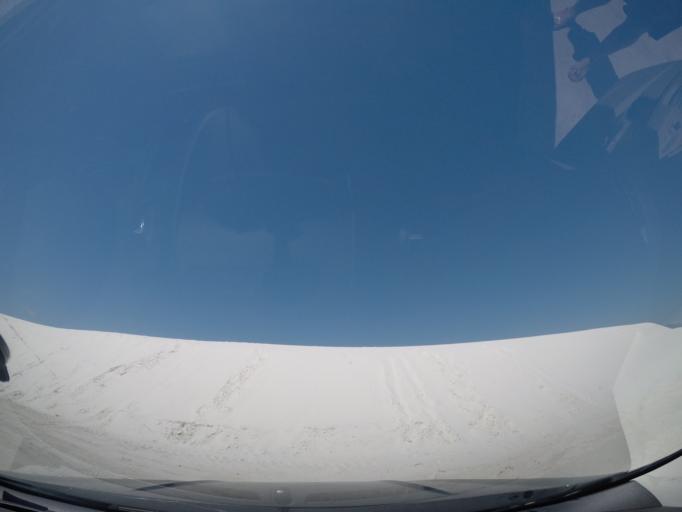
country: US
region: New Mexico
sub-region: Otero County
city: Holloman Air Force Base
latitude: 32.8190
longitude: -106.2652
